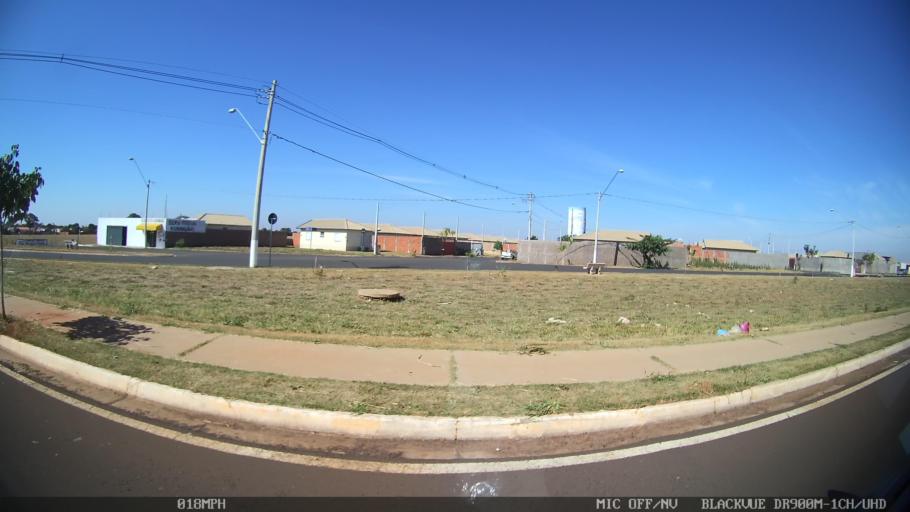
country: BR
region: Sao Paulo
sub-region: Sao Jose Do Rio Preto
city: Sao Jose do Rio Preto
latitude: -20.7468
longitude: -49.4362
